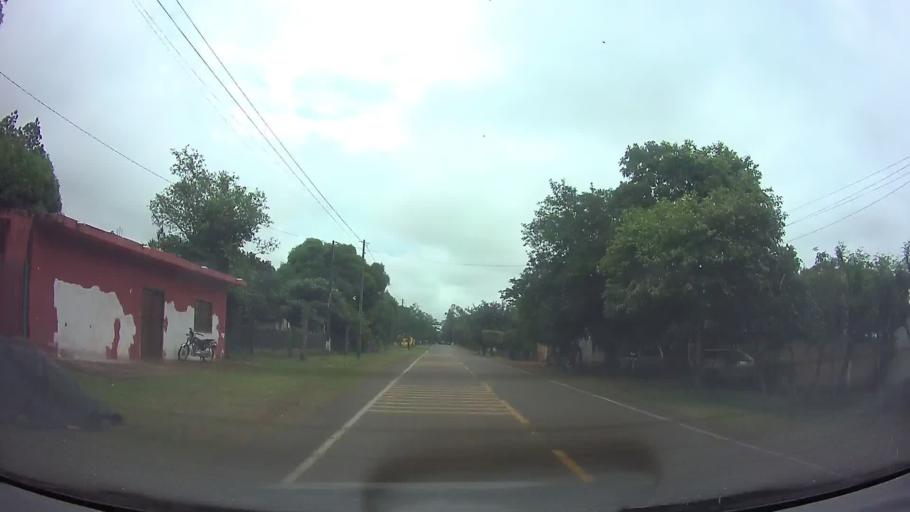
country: PY
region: Paraguari
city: Acahay
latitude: -25.9178
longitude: -57.1119
